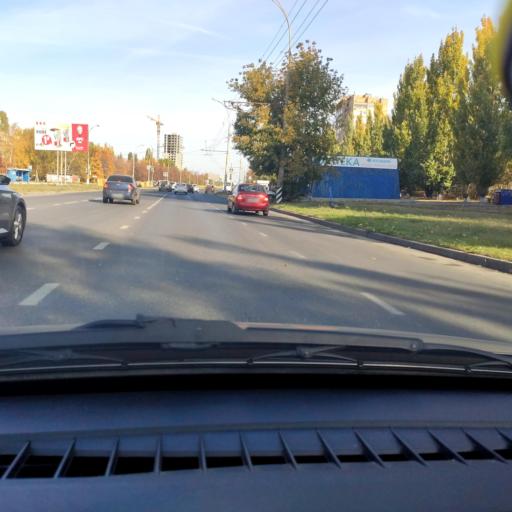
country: RU
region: Samara
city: Tol'yatti
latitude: 53.5207
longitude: 49.2956
